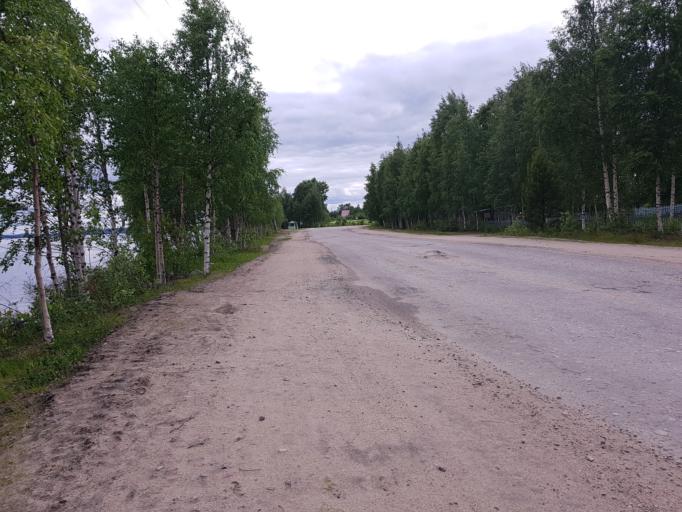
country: RU
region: Republic of Karelia
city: Kalevala
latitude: 65.1942
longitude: 31.1813
